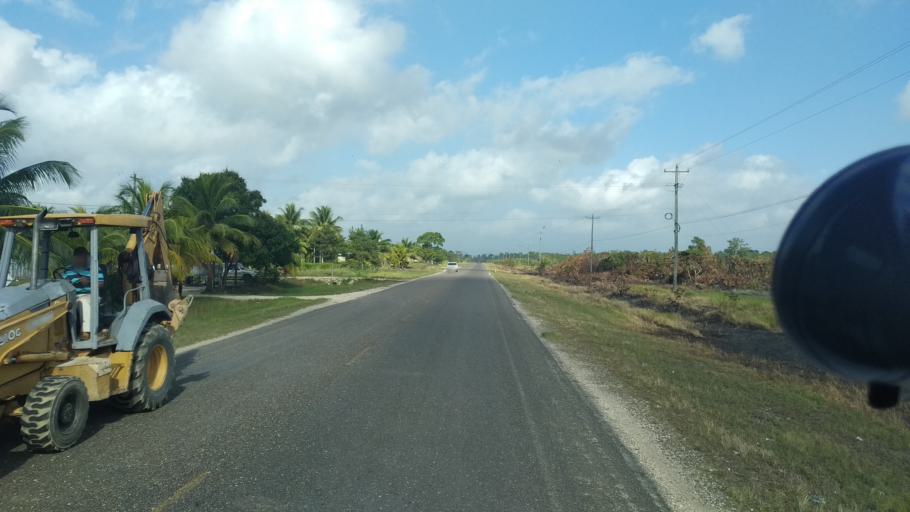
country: BZ
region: Stann Creek
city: Placencia
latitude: 16.5131
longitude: -88.5436
